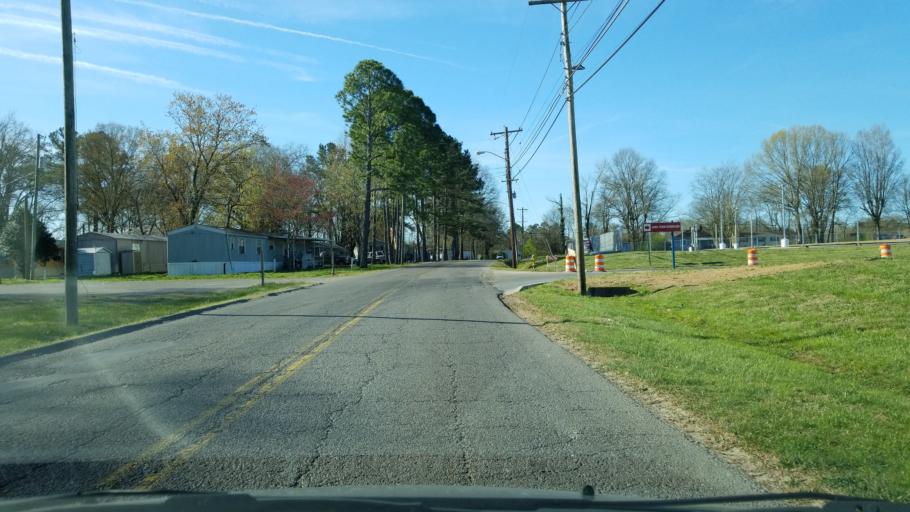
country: US
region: Tennessee
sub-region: Hamilton County
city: East Brainerd
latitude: 35.0307
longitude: -85.1948
